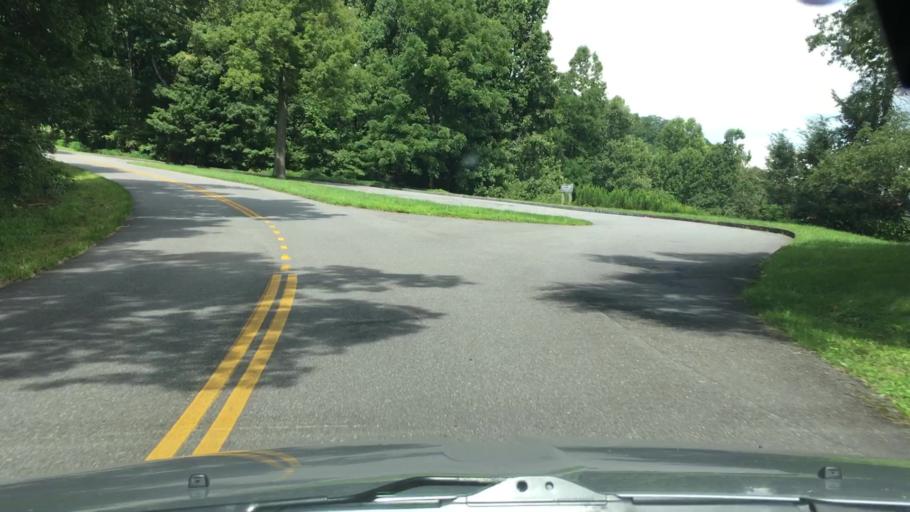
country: US
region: North Carolina
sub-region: McDowell County
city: West Marion
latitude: 35.7561
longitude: -82.1770
